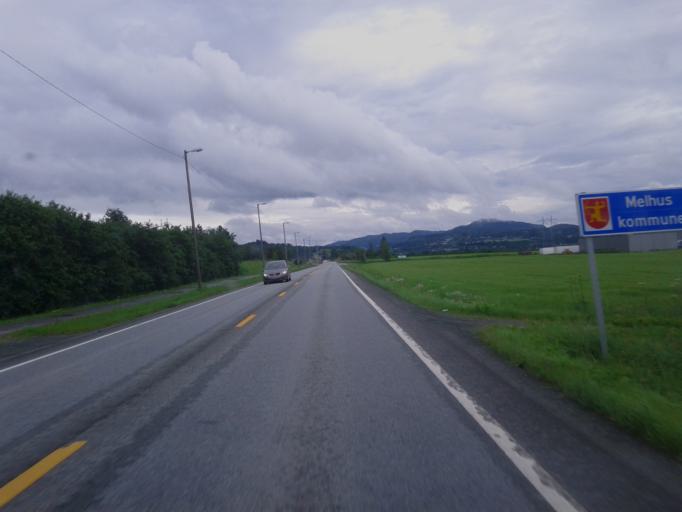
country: NO
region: Sor-Trondelag
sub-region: Melhus
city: Melhus
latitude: 63.3119
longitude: 10.2930
